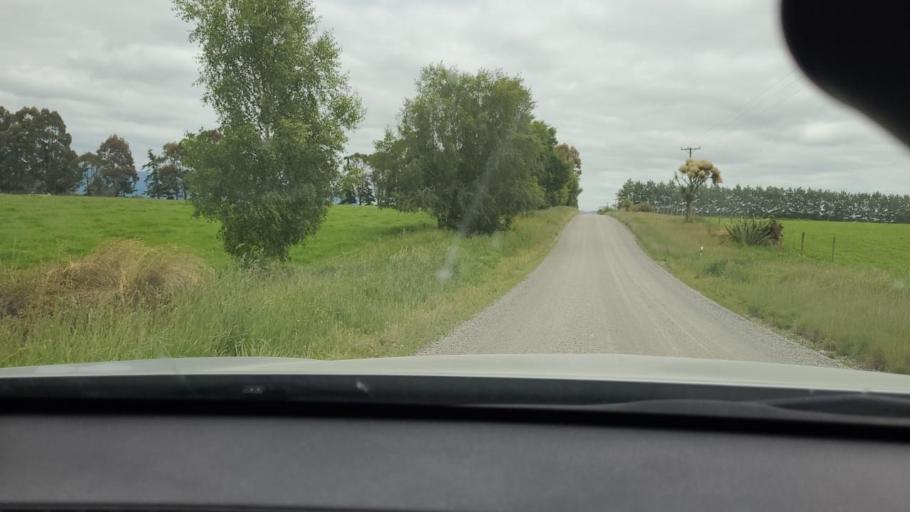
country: NZ
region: Southland
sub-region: Southland District
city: Riverton
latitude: -46.0658
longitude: 168.0212
